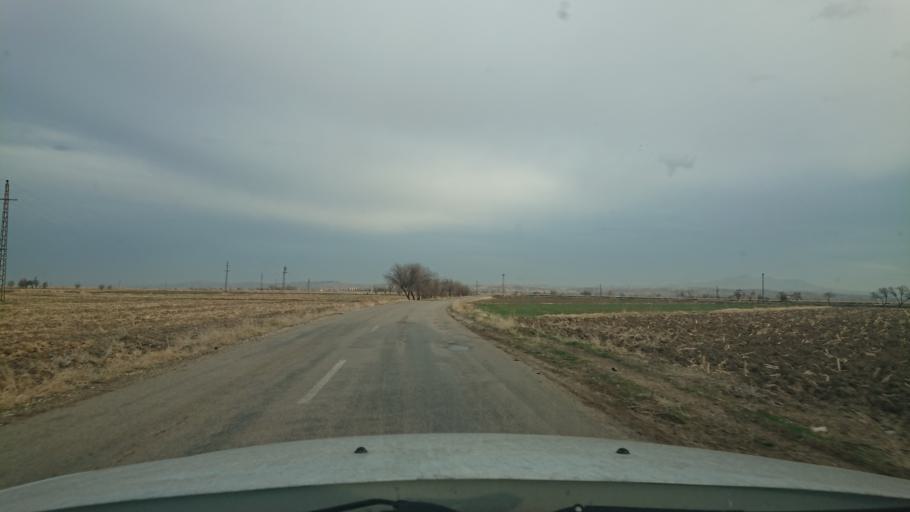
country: TR
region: Aksaray
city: Yesilova
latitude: 38.4293
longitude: 33.8354
